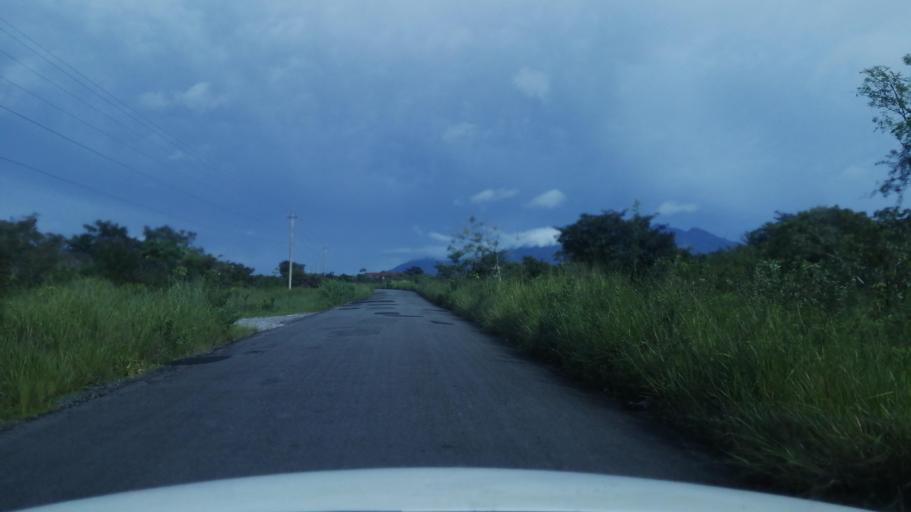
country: PA
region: Chiriqui
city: Potrerillos Abajo
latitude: 8.6682
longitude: -82.4303
